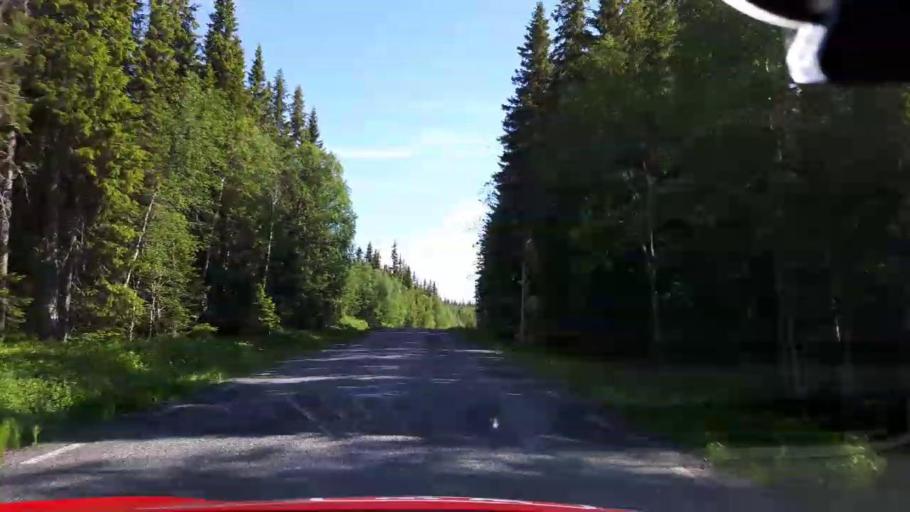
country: SE
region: Jaemtland
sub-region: Krokoms Kommun
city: Valla
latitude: 63.7459
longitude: 14.1186
